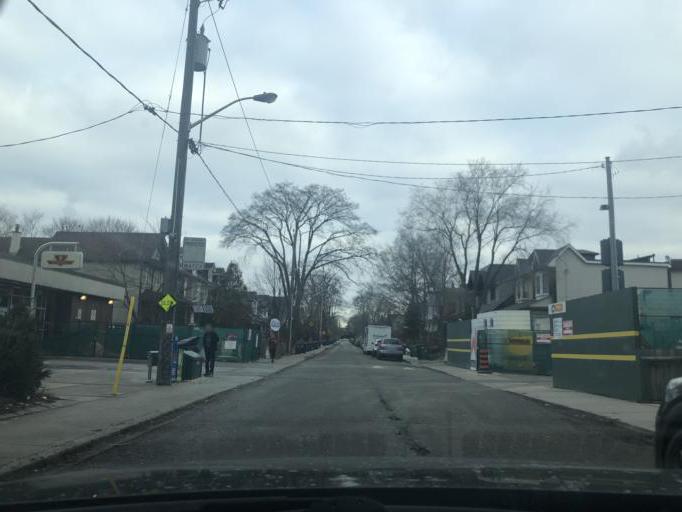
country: CA
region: Ontario
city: Toronto
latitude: 43.6780
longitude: -79.3522
